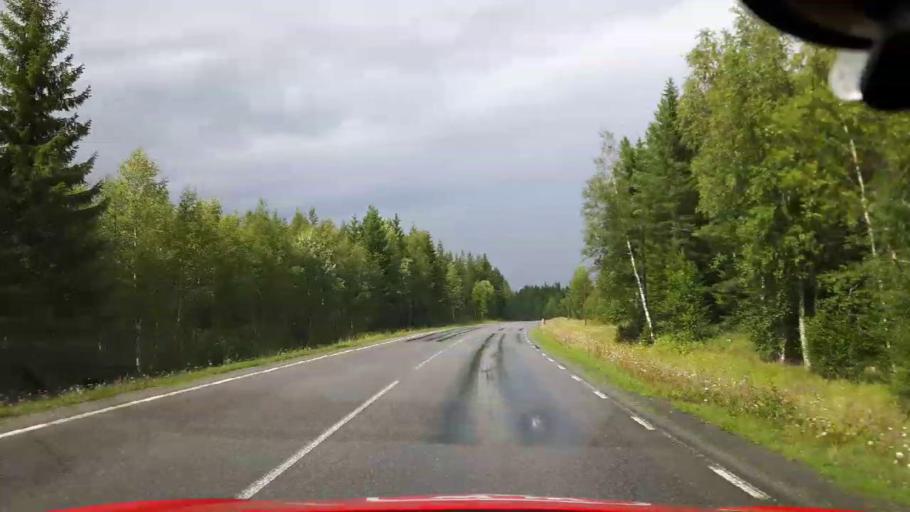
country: SE
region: Jaemtland
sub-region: Krokoms Kommun
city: Krokom
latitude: 63.3363
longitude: 14.2773
